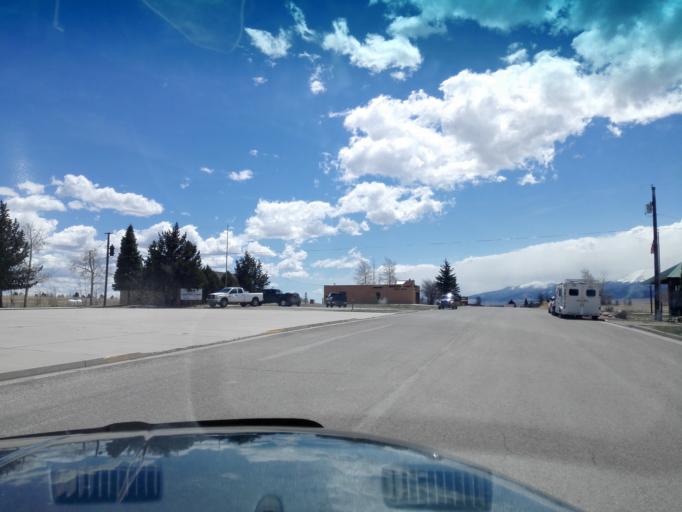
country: US
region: Colorado
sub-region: Custer County
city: Westcliffe
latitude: 38.1358
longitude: -105.4592
